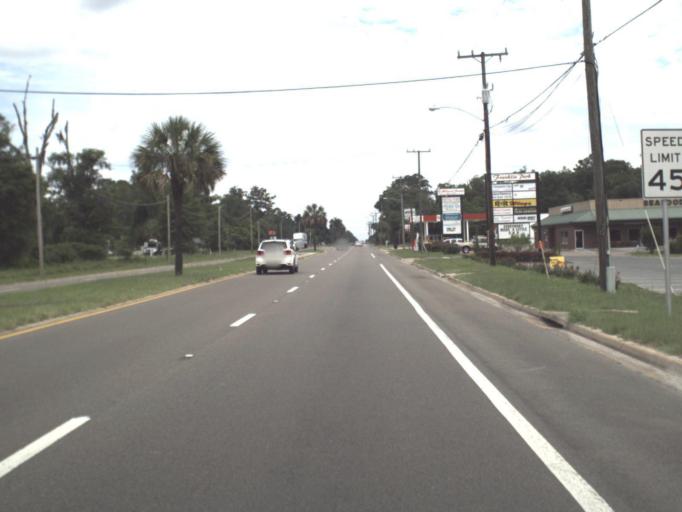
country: US
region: Florida
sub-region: Nassau County
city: Hilliard
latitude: 30.6934
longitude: -81.9193
